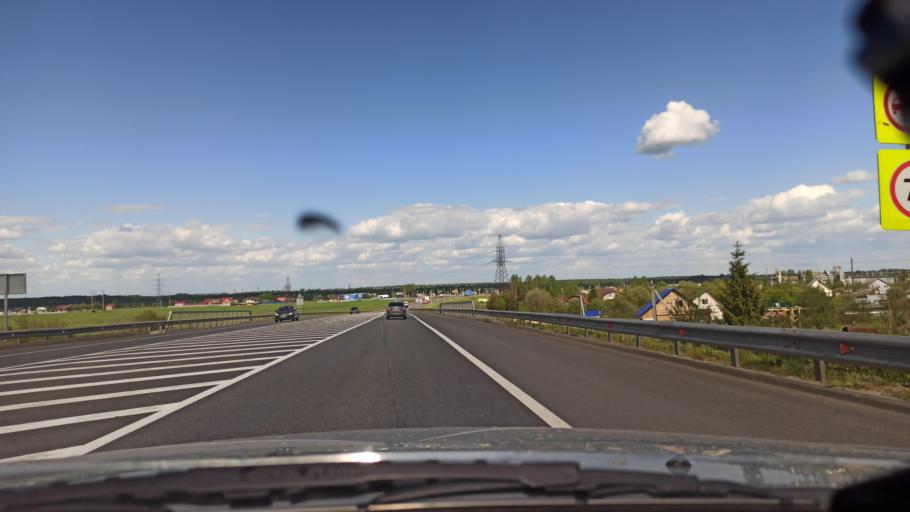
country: RU
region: Vologda
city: Vologda
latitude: 59.2838
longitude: 39.8442
